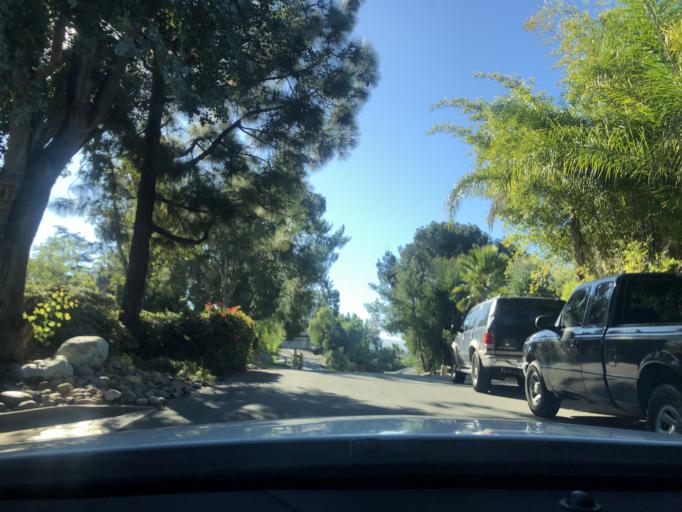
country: US
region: California
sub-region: San Diego County
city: Rancho San Diego
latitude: 32.7683
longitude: -116.9397
